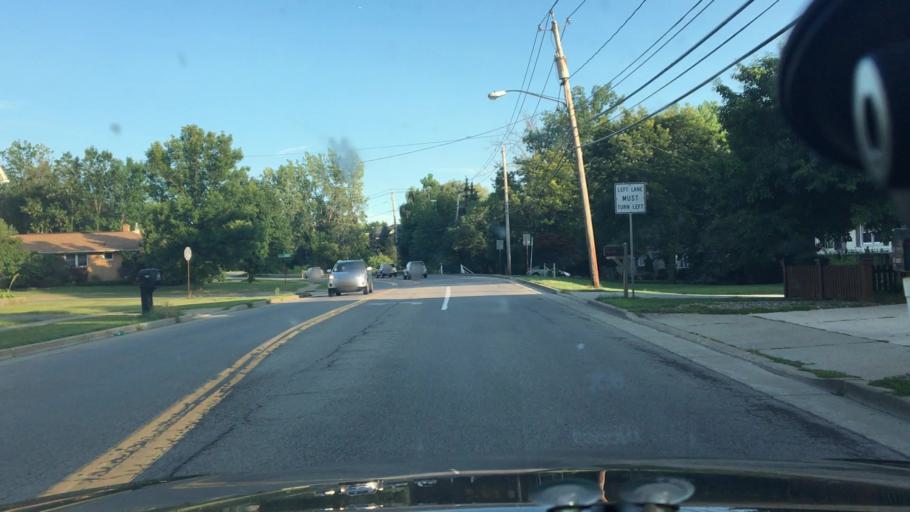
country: US
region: New York
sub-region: Erie County
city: Amherst
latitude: 43.0050
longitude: -78.7630
